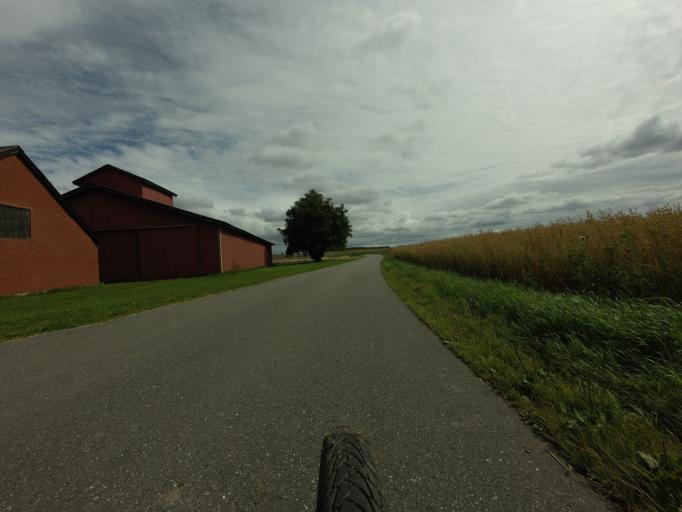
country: DK
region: Central Jutland
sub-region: Syddjurs Kommune
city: Ryomgard
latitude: 56.4023
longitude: 10.5437
